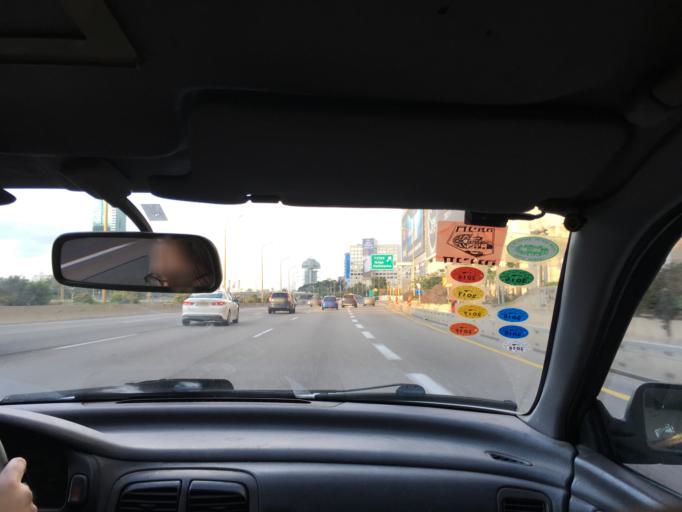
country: IL
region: Tel Aviv
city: Ramat Gan
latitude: 32.0849
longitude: 34.7994
